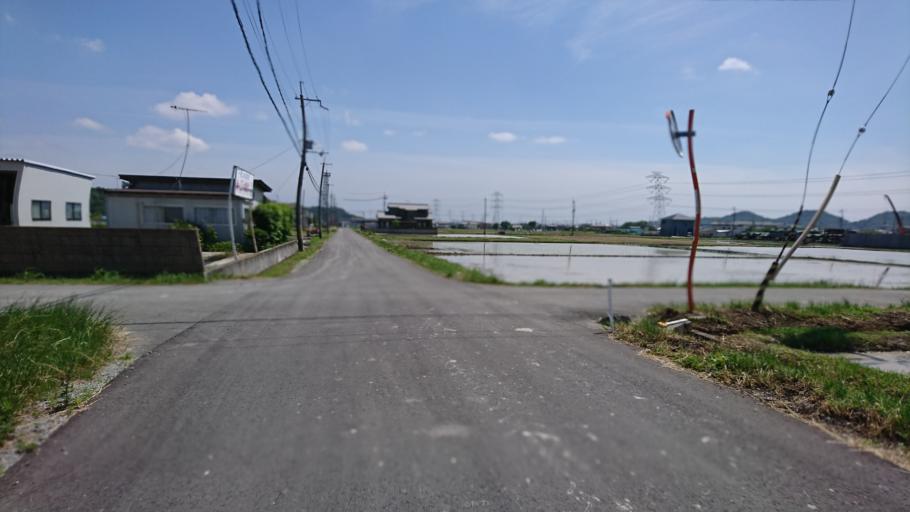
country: JP
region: Hyogo
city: Kakogawacho-honmachi
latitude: 34.8027
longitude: 134.7858
